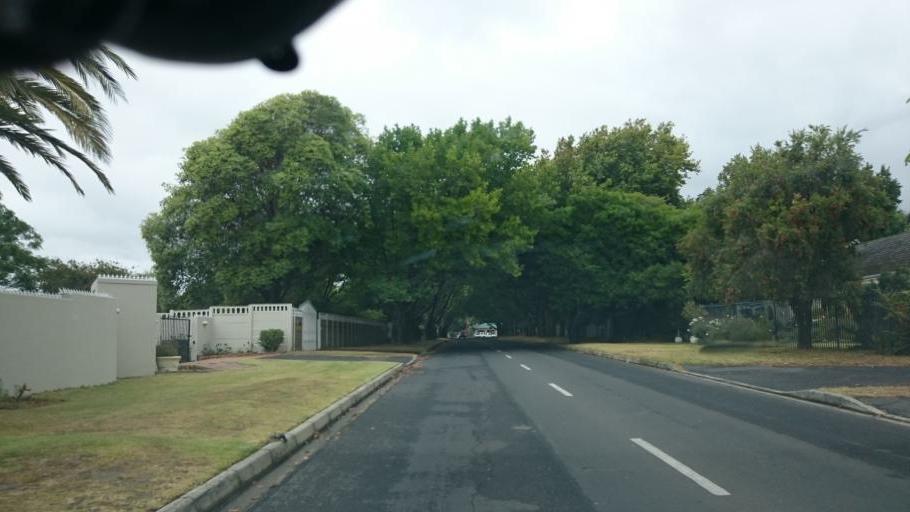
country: ZA
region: Western Cape
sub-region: City of Cape Town
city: Bergvliet
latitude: -34.0272
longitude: 18.4508
